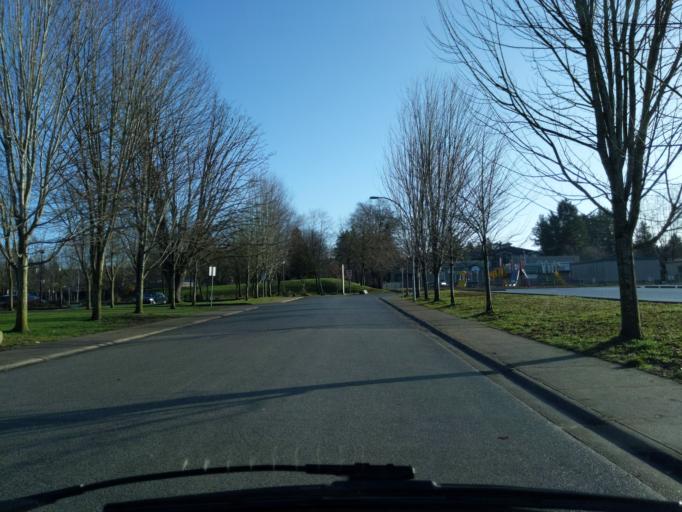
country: CA
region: British Columbia
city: Pitt Meadows
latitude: 49.2201
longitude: -122.6924
